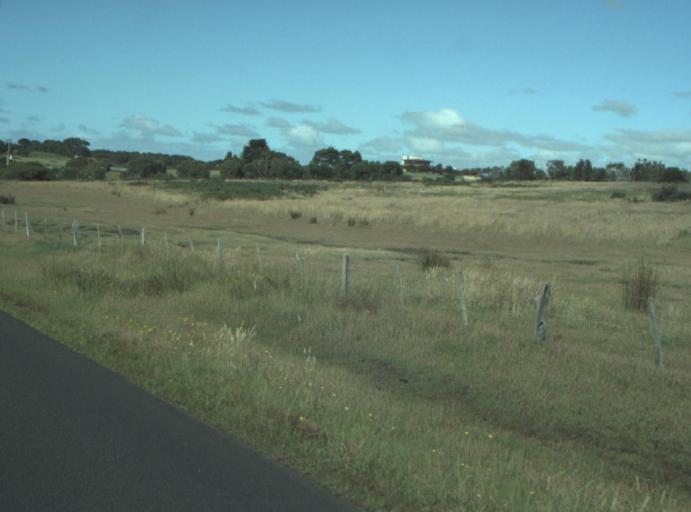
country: AU
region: Victoria
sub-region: Greater Geelong
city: Clifton Springs
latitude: -38.2288
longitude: 144.5836
